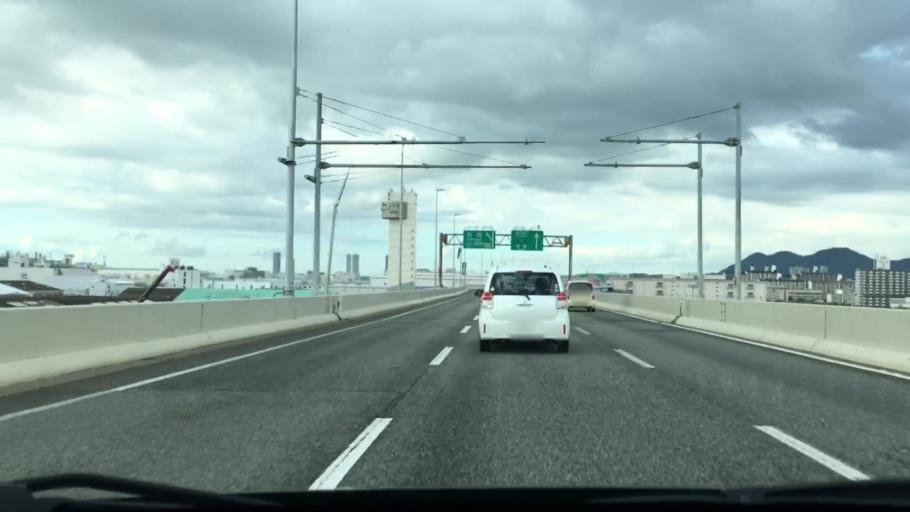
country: JP
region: Fukuoka
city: Fukuoka-shi
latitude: 33.6191
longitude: 130.4125
